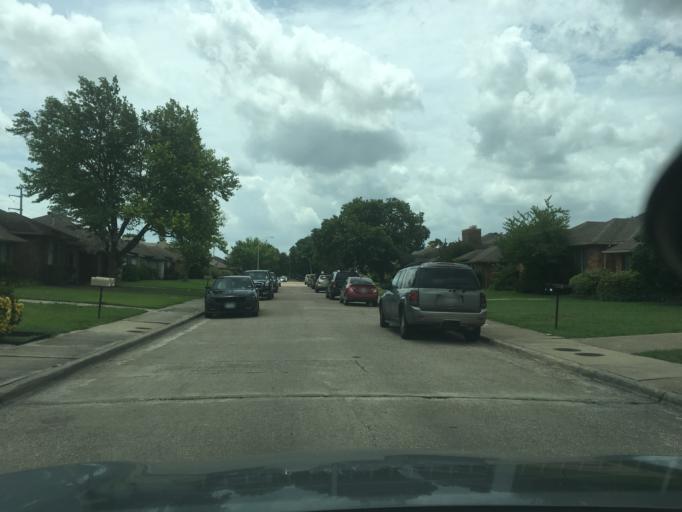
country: US
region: Texas
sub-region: Dallas County
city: Richardson
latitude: 32.9298
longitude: -96.7136
